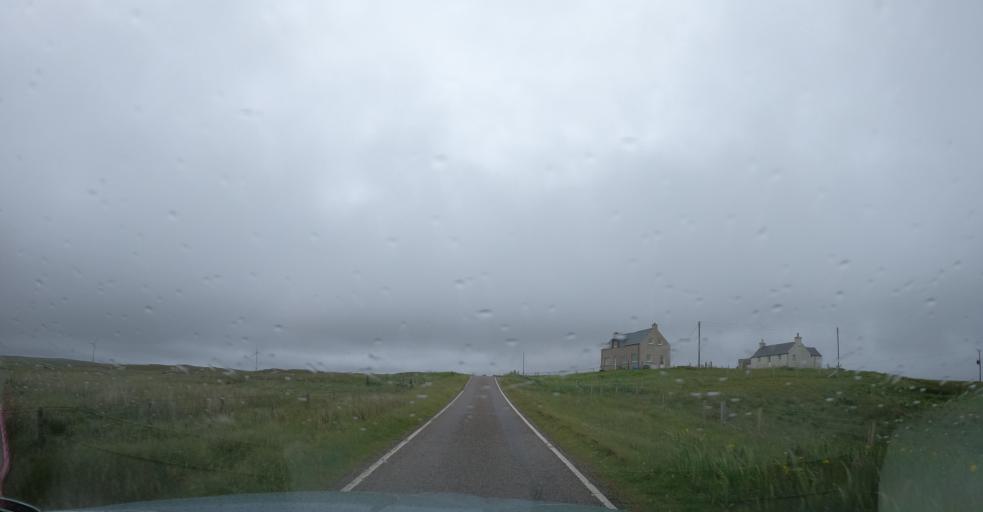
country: GB
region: Scotland
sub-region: Eilean Siar
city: Isle of North Uist
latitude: 57.5559
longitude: -7.3496
